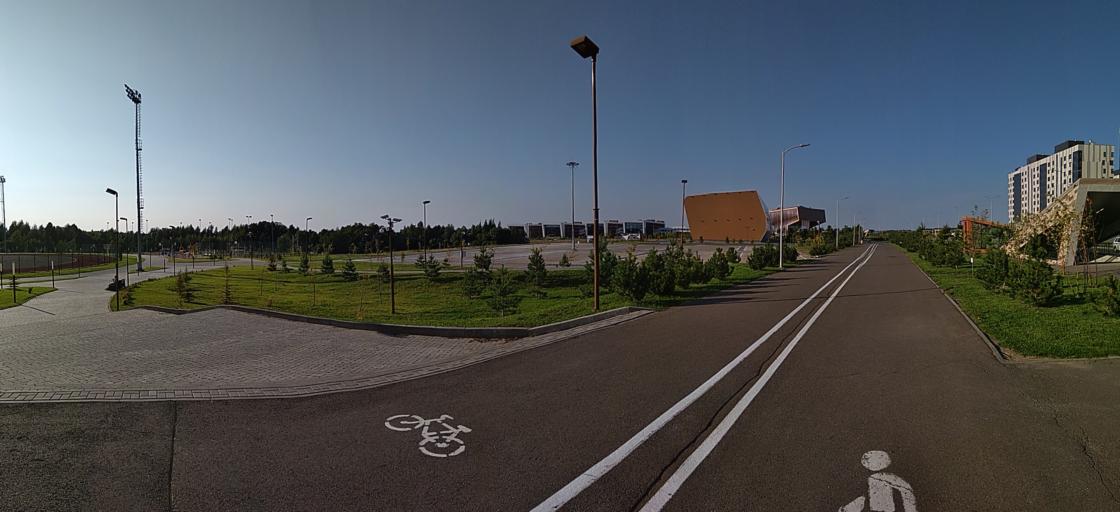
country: RU
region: Tatarstan
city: Sviyazhsk
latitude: 55.7491
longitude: 48.7424
